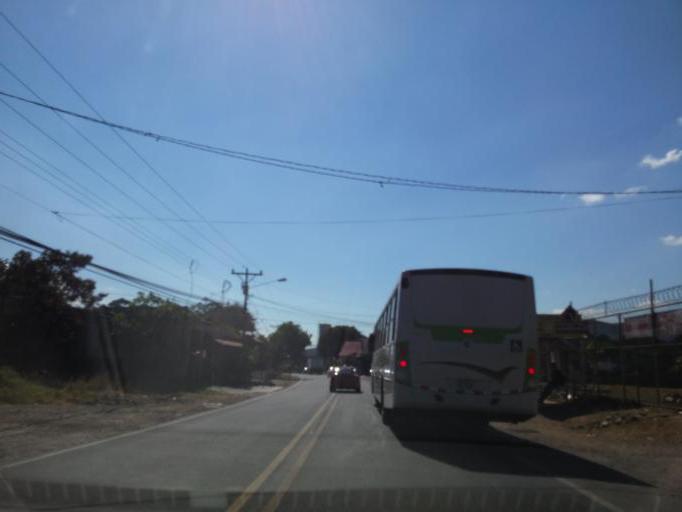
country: CR
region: Alajuela
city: Alajuela
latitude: 10.0358
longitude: -84.1990
